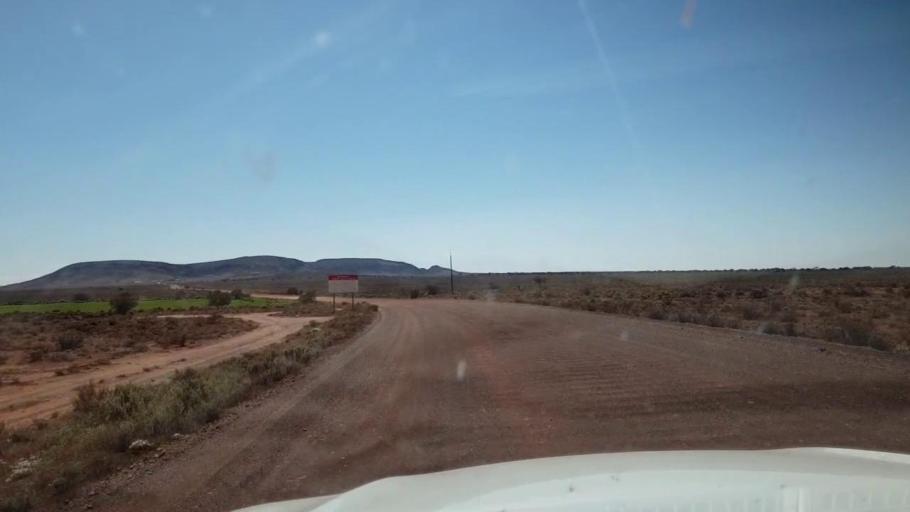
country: AU
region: South Australia
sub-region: Whyalla
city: Whyalla
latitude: -32.7170
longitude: 137.1434
